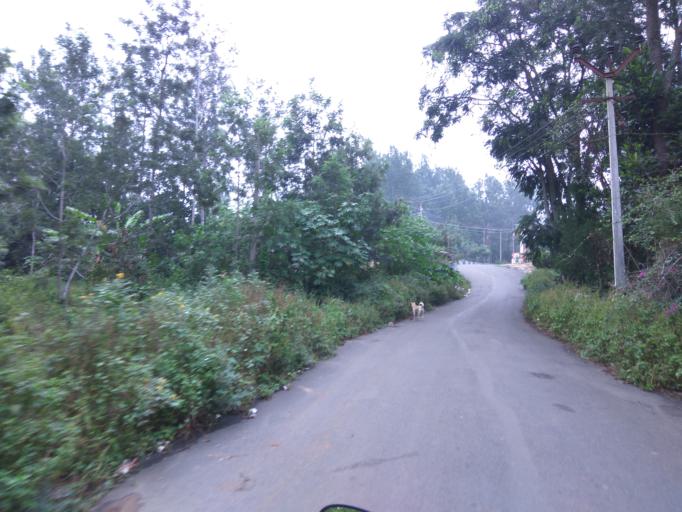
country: IN
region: Tamil Nadu
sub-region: Salem
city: Salem
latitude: 11.7682
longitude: 78.2385
